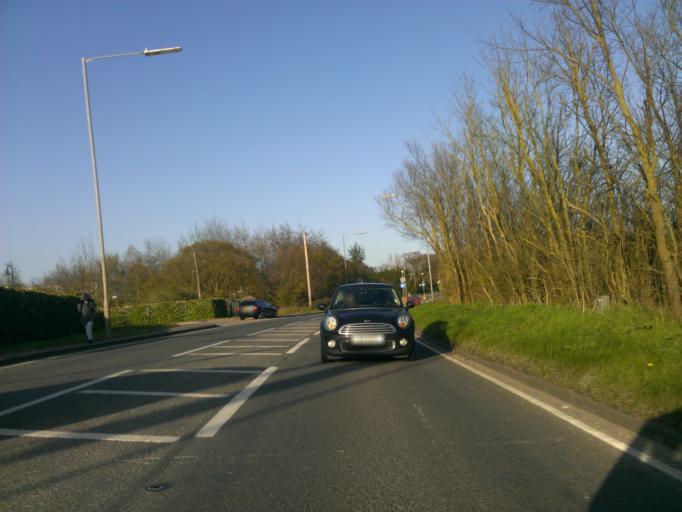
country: GB
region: England
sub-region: Essex
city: Great Bentley
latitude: 51.8706
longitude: 1.0424
